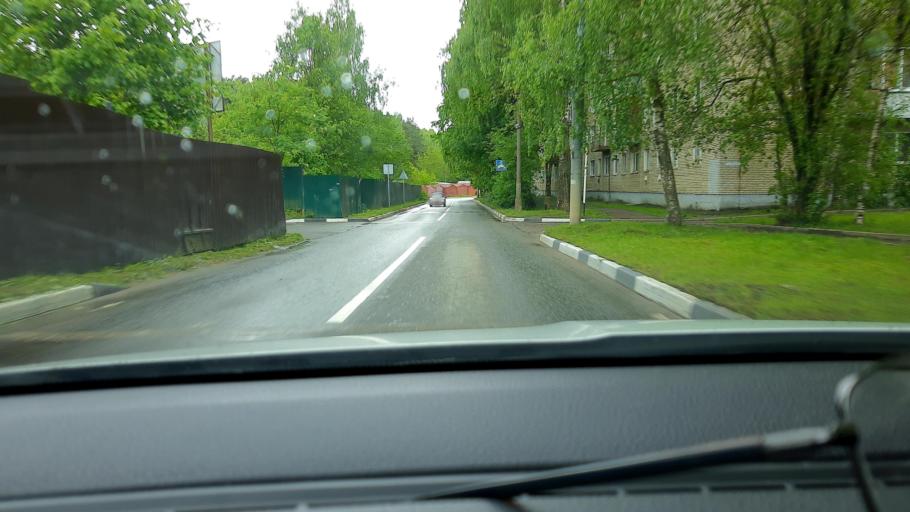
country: RU
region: Moskovskaya
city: Zvenigorod
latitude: 55.7419
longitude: 36.8679
